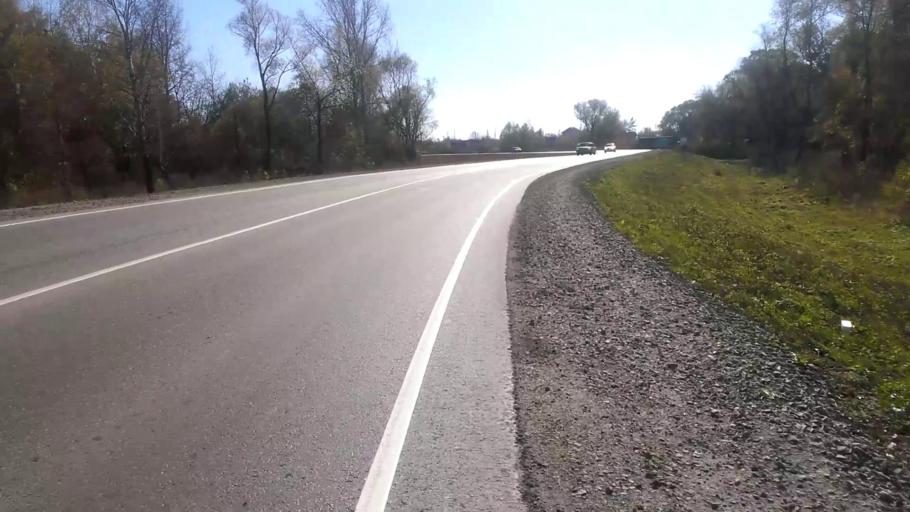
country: RU
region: Altai Krai
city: Sannikovo
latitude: 53.3233
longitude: 83.9429
